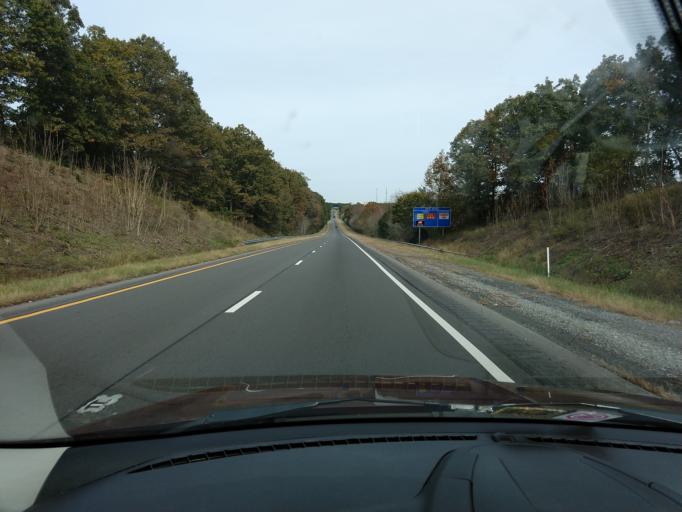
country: US
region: Virginia
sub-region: Pittsylvania County
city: Gretna
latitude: 36.9392
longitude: -79.3765
